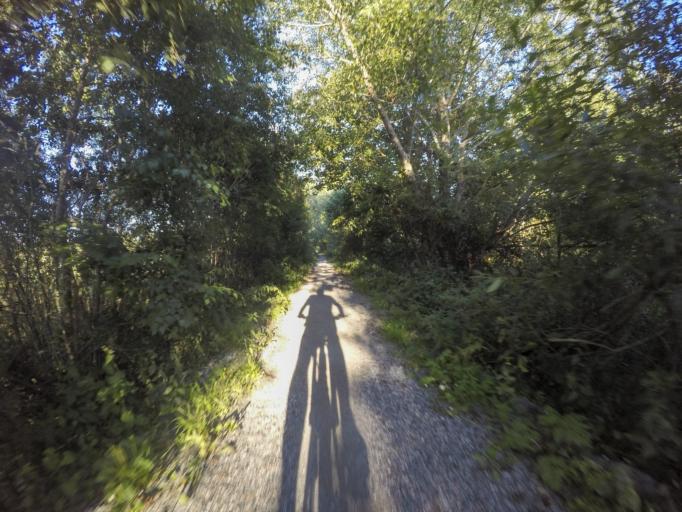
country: SE
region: Vaestmanland
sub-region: Vasteras
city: Vasteras
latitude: 59.5742
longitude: 16.6352
